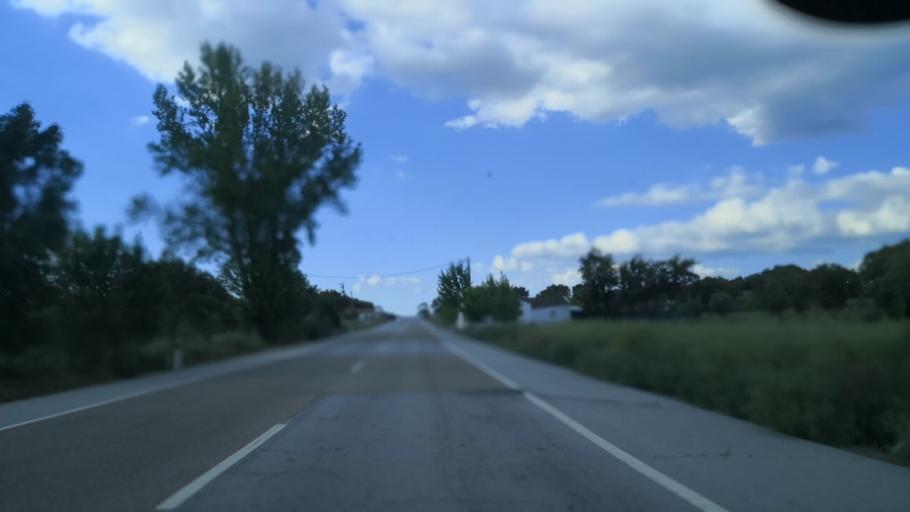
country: PT
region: Portalegre
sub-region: Portalegre
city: Urra
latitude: 39.2345
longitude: -7.4531
